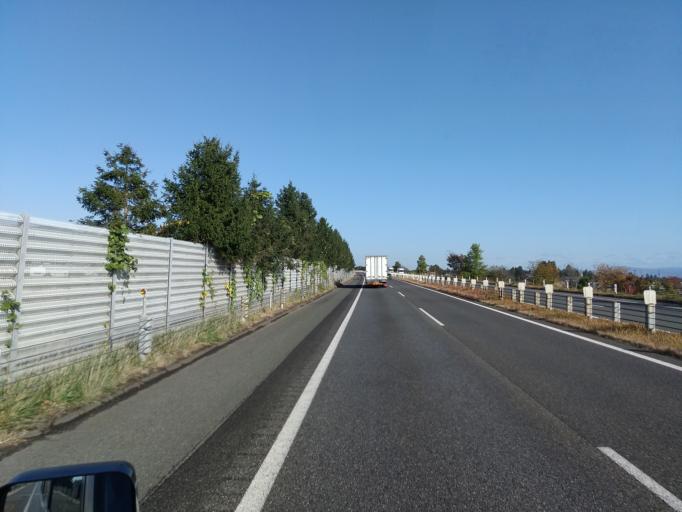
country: JP
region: Iwate
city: Hanamaki
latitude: 39.4765
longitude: 141.1099
